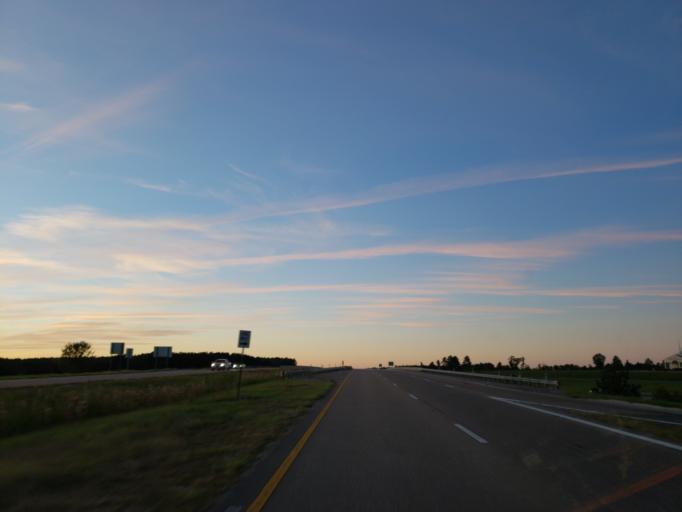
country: US
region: Mississippi
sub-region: Wayne County
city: Waynesboro
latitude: 31.7065
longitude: -88.6252
